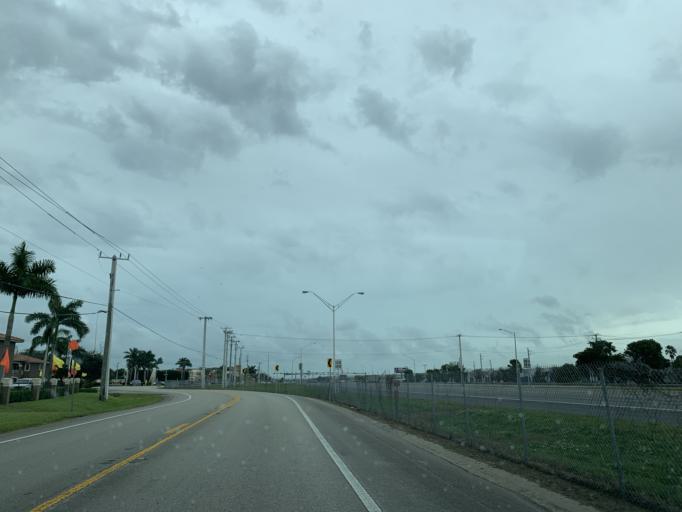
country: US
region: Florida
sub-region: Miami-Dade County
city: Hialeah Gardens
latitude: 25.8688
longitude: -80.3409
